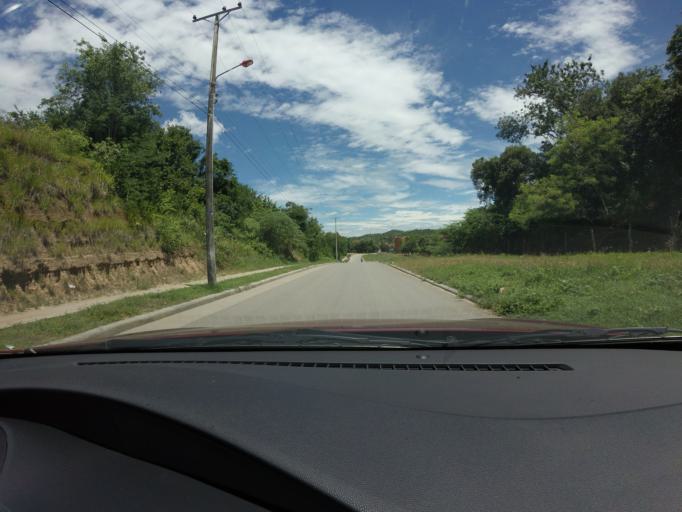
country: CO
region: Cundinamarca
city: Ricaurte
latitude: 4.2722
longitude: -74.7735
